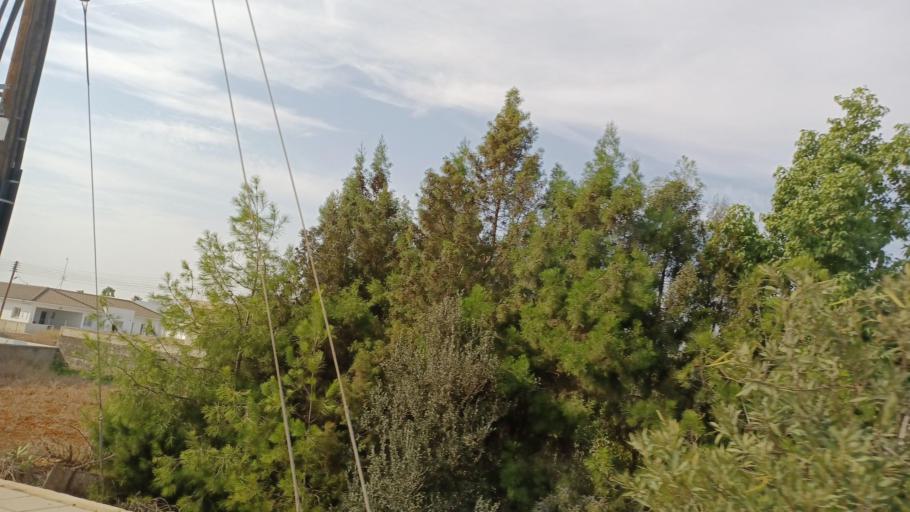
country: CY
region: Ammochostos
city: Frenaros
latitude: 35.0367
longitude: 33.9175
